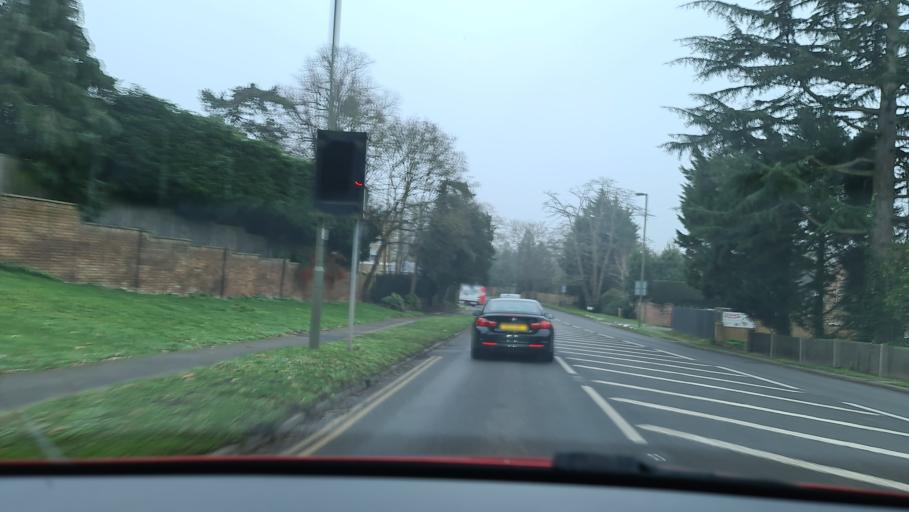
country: GB
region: England
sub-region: Surrey
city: Esher
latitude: 51.3625
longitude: -0.3641
